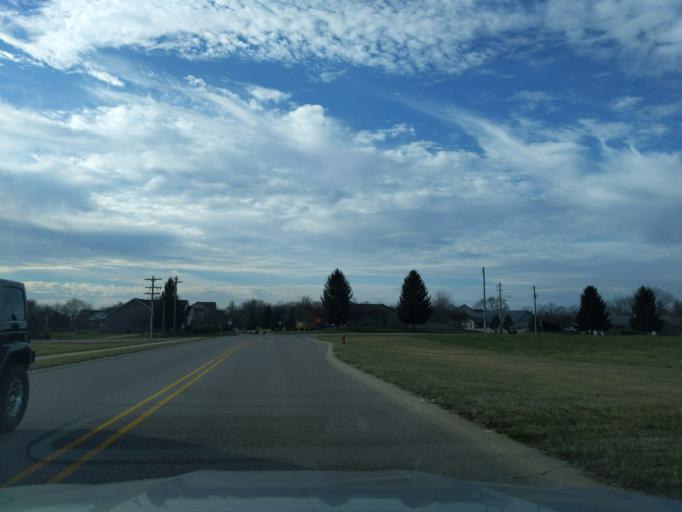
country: US
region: Indiana
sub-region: Decatur County
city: Greensburg
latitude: 39.3201
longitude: -85.4690
